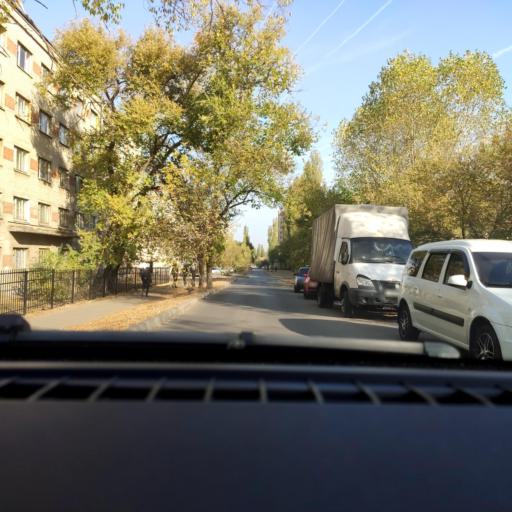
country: RU
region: Voronezj
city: Maslovka
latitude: 51.6109
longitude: 39.2323
